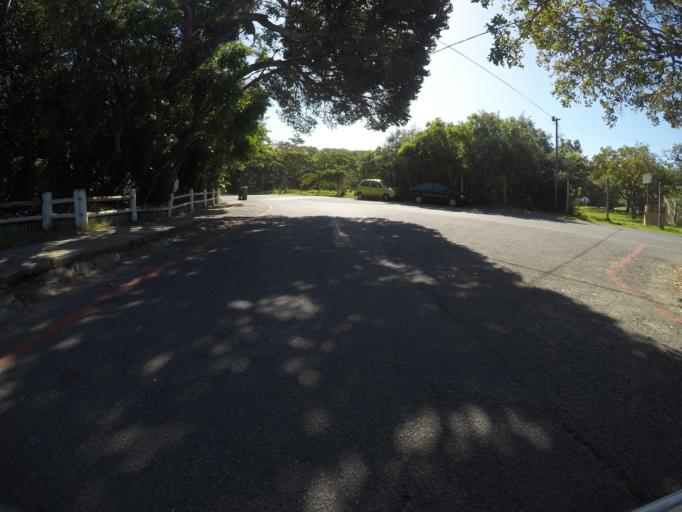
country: ZA
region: Eastern Cape
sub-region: Buffalo City Metropolitan Municipality
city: East London
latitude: -32.9858
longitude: 27.9479
